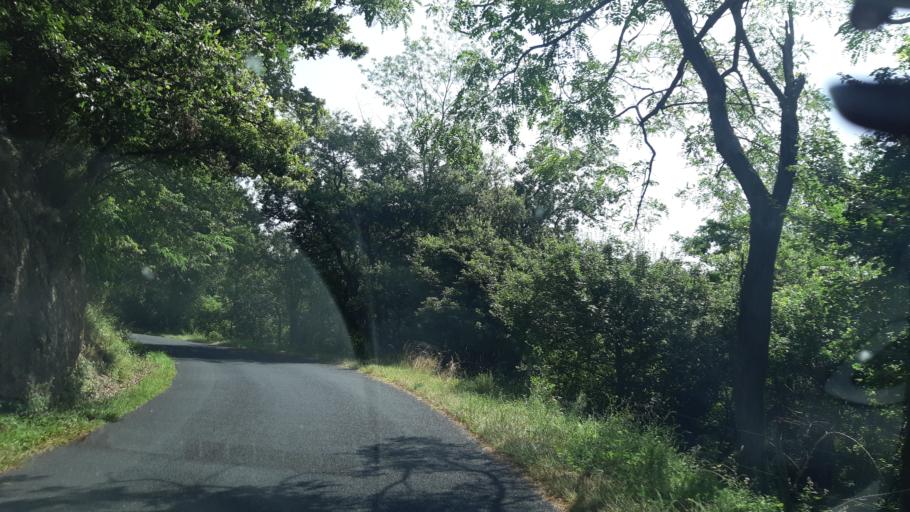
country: FR
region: Languedoc-Roussillon
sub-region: Departement des Pyrenees-Orientales
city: Arles
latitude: 42.5242
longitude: 2.6133
